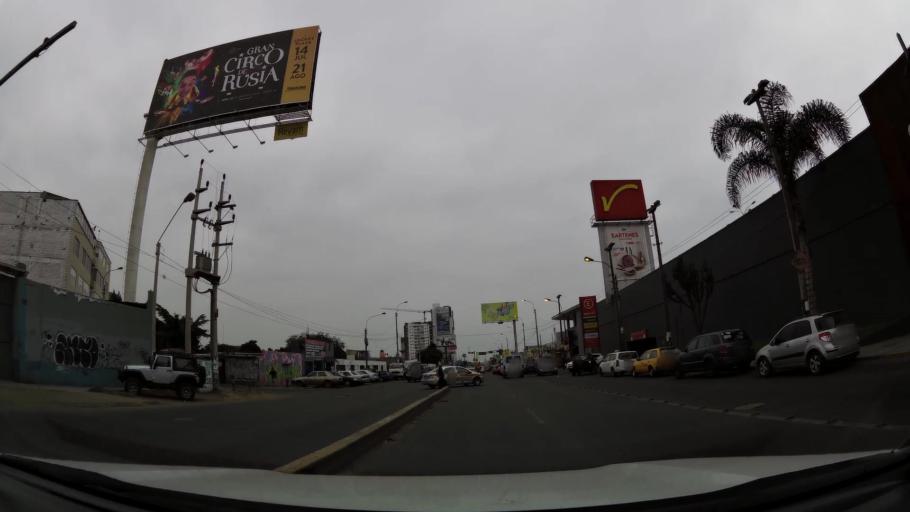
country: PE
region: Lima
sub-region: Lima
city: Surco
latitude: -12.1344
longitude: -77.0180
